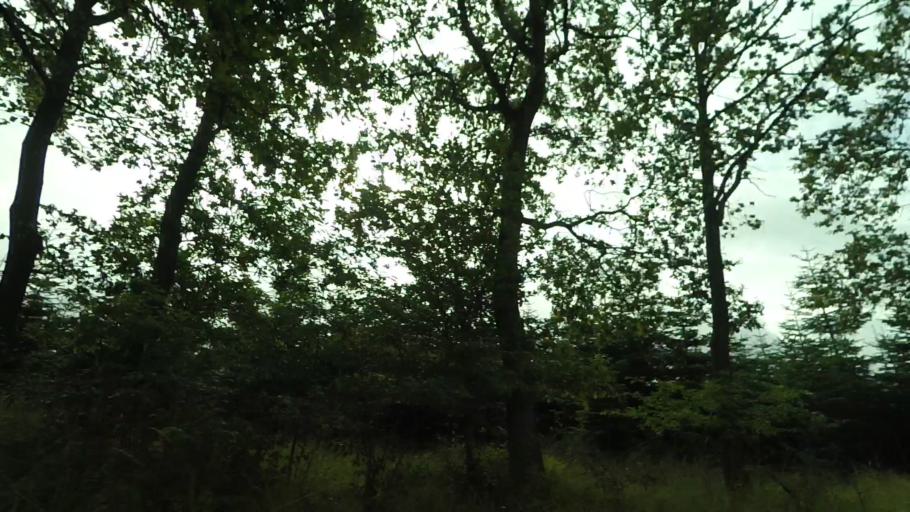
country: DK
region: Central Jutland
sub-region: Syddjurs Kommune
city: Ronde
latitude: 56.3396
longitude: 10.4844
